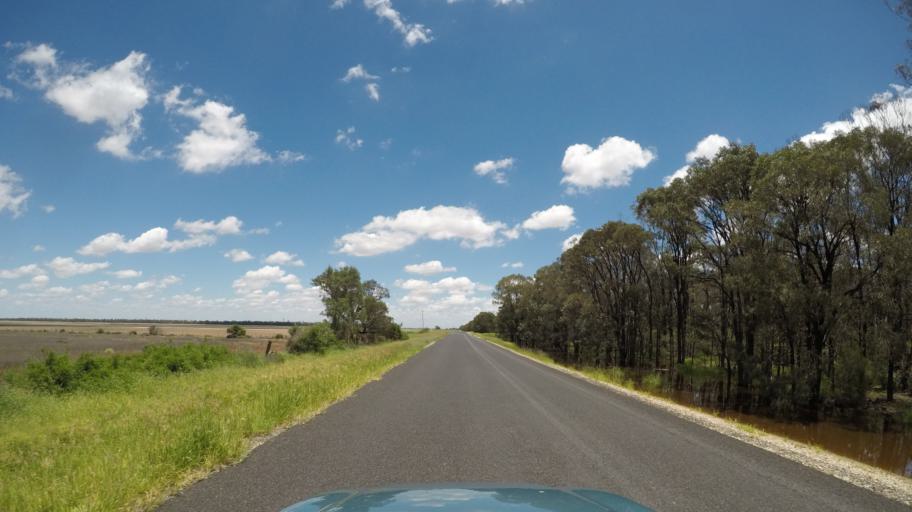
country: AU
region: Queensland
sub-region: Goondiwindi
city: Goondiwindi
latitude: -28.1602
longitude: 150.4027
